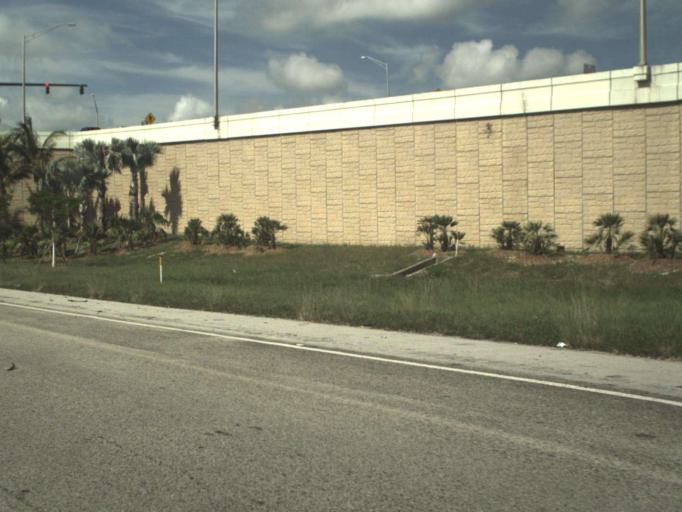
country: US
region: Florida
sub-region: Palm Beach County
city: Lake Clarke Shores
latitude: 26.6773
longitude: -80.0699
